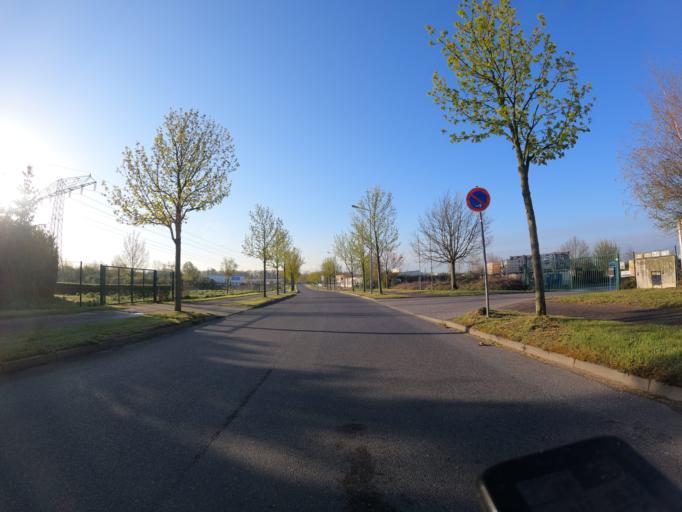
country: DE
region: Brandenburg
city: Neuenhagen
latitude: 52.5330
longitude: 13.7129
